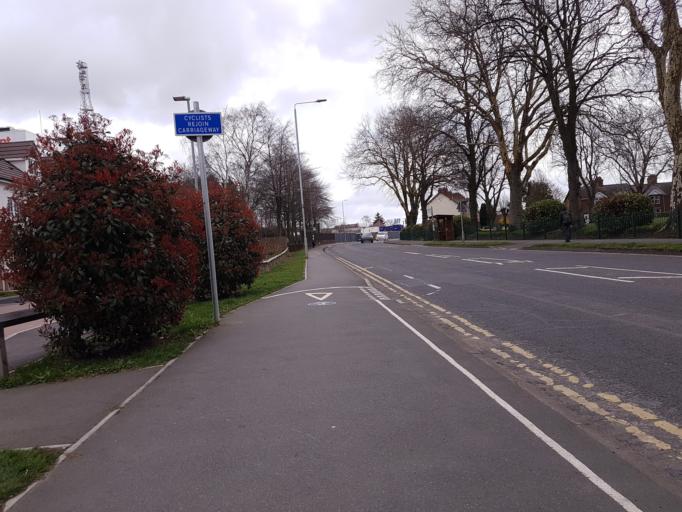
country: GB
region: England
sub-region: Leicestershire
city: Hinckley
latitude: 52.5387
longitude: -1.3808
